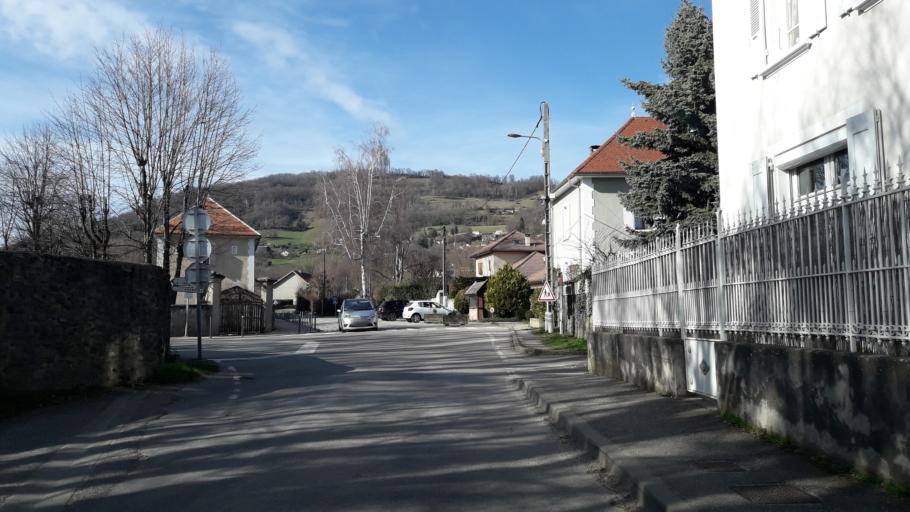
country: FR
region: Rhone-Alpes
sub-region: Departement de l'Isere
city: Herbeys
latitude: 45.1396
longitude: 5.7926
